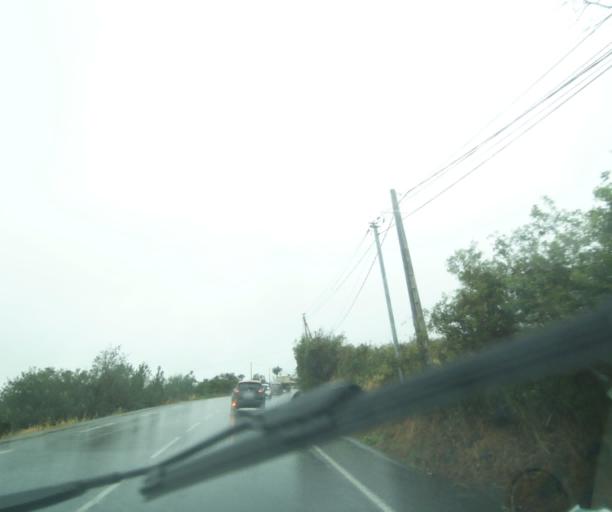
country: RE
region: Reunion
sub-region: Reunion
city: Saint-Paul
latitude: -21.0350
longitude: 55.2730
